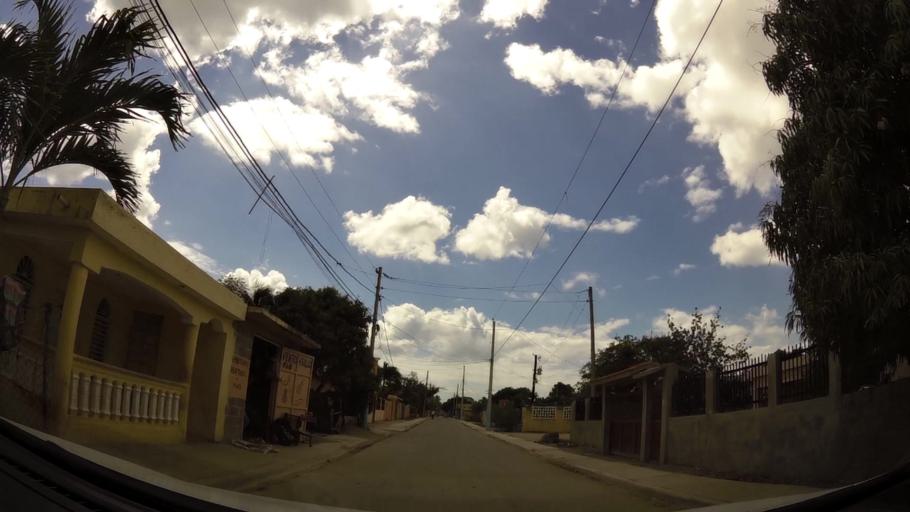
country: DO
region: Santo Domingo
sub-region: Santo Domingo
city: Boca Chica
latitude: 18.4525
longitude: -69.6522
